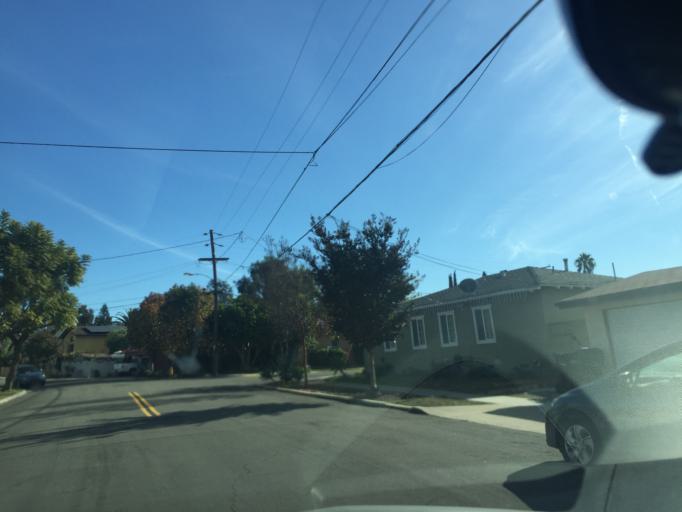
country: US
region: California
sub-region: San Diego County
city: Lemon Grove
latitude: 32.7619
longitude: -117.0819
